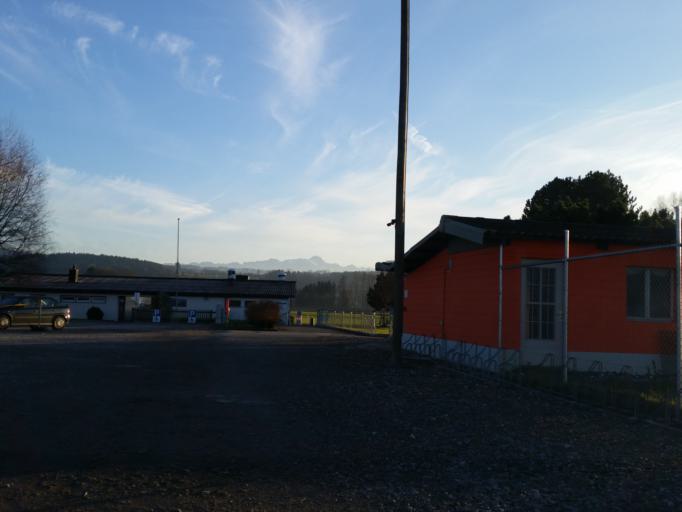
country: CH
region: Thurgau
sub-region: Weinfelden District
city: Erlen
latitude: 47.5101
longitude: 9.2604
